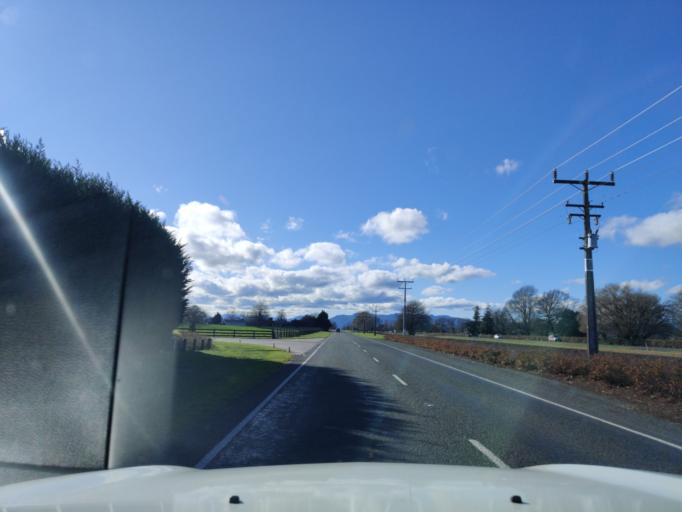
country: NZ
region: Waikato
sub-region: Matamata-Piako District
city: Matamata
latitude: -37.8490
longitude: 175.7598
